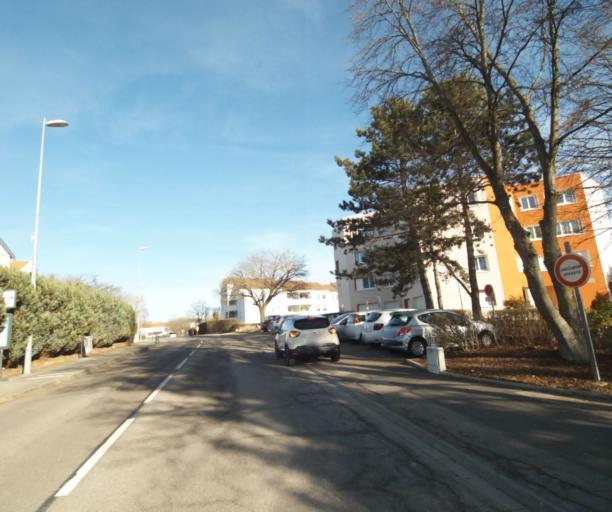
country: FR
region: Lorraine
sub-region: Departement de Meurthe-et-Moselle
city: Chavigny
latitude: 48.6562
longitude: 6.1126
